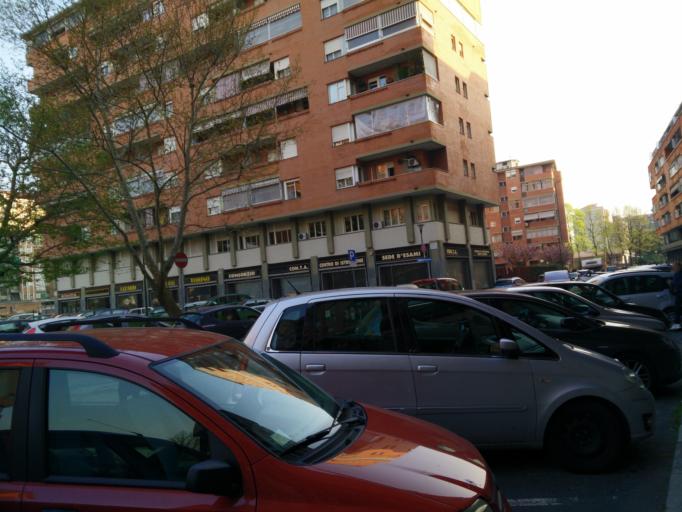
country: IT
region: Piedmont
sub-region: Provincia di Torino
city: Nichelino
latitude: 45.0188
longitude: 7.6450
